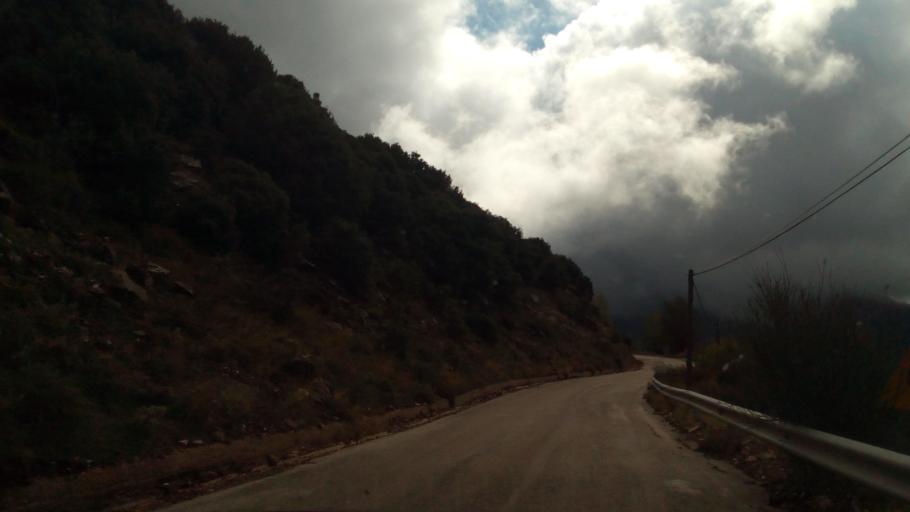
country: GR
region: West Greece
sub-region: Nomos Aitolias kai Akarnanias
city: Nafpaktos
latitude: 38.5314
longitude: 21.8269
